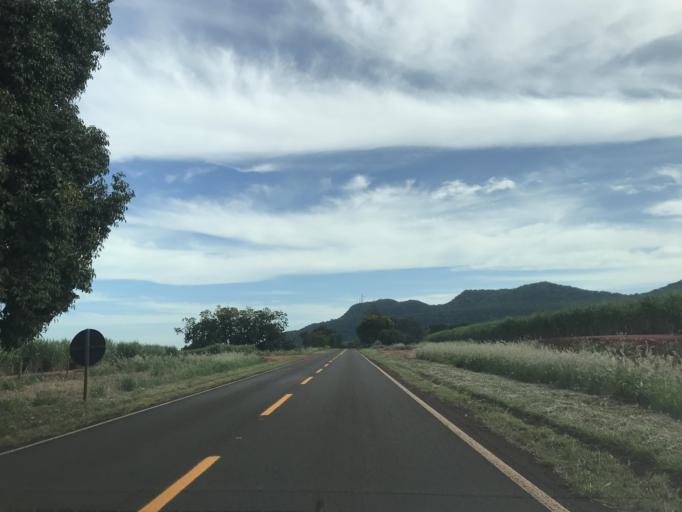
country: BR
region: Parana
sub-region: Terra Rica
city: Terra Rica
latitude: -22.8049
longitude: -52.6537
